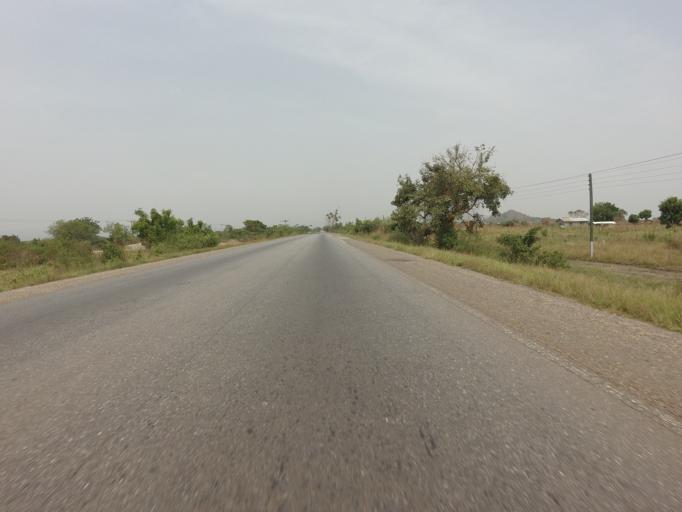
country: GH
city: Akropong
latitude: 6.0311
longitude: 0.0489
